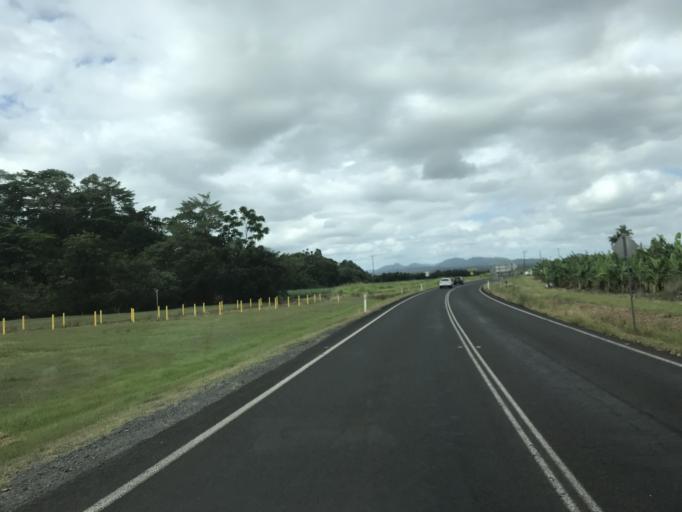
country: AU
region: Queensland
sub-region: Cassowary Coast
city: Innisfail
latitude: -17.5796
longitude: 146.0037
